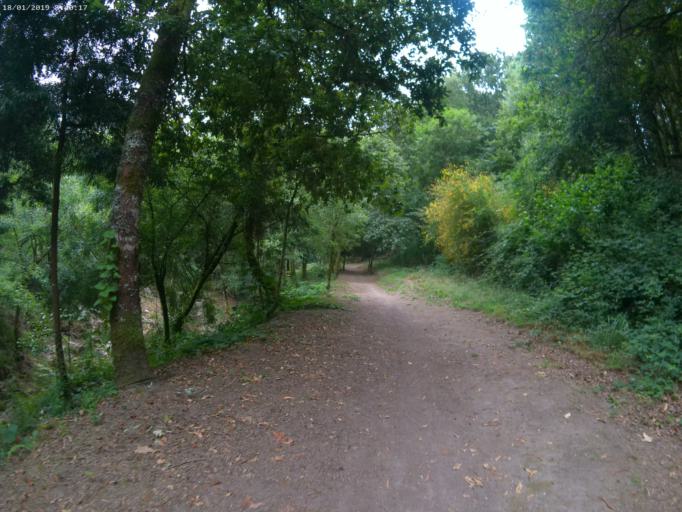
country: PT
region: Viana do Castelo
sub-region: Ponte da Barca
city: Ponte da Barca
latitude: 41.8095
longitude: -8.4303
